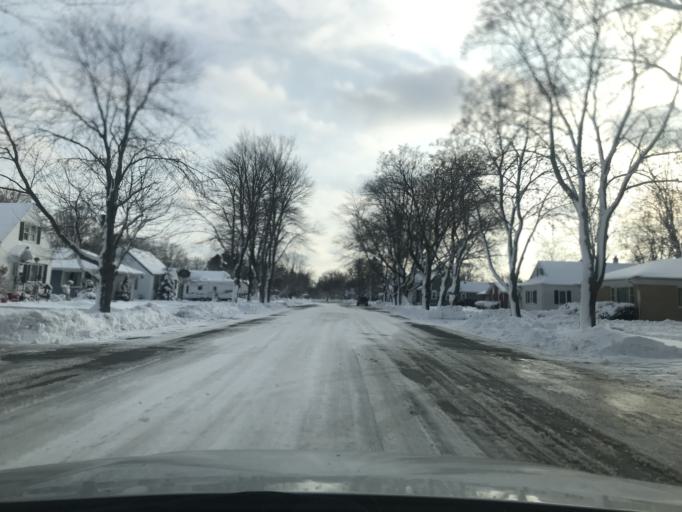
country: US
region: Wisconsin
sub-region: Marinette County
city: Peshtigo
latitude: 45.0523
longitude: -87.7550
